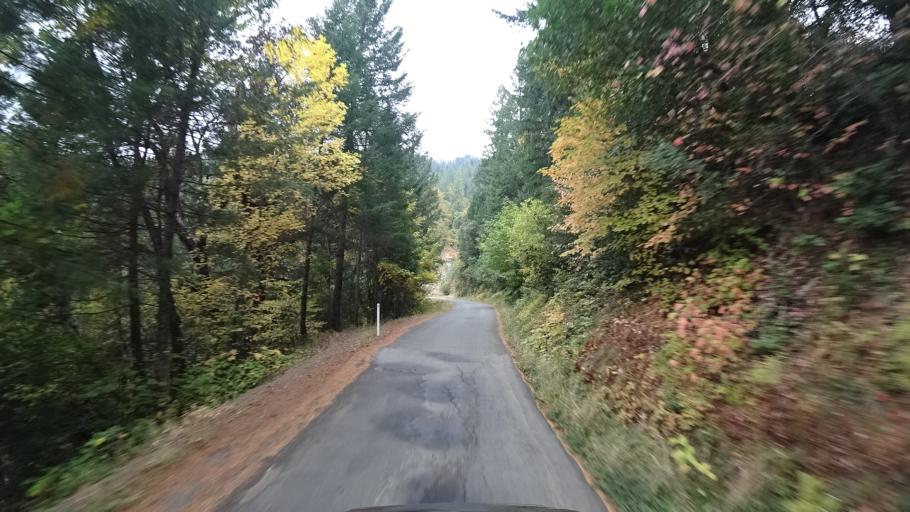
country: US
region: California
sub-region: Siskiyou County
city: Happy Camp
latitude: 41.7775
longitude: -123.3811
